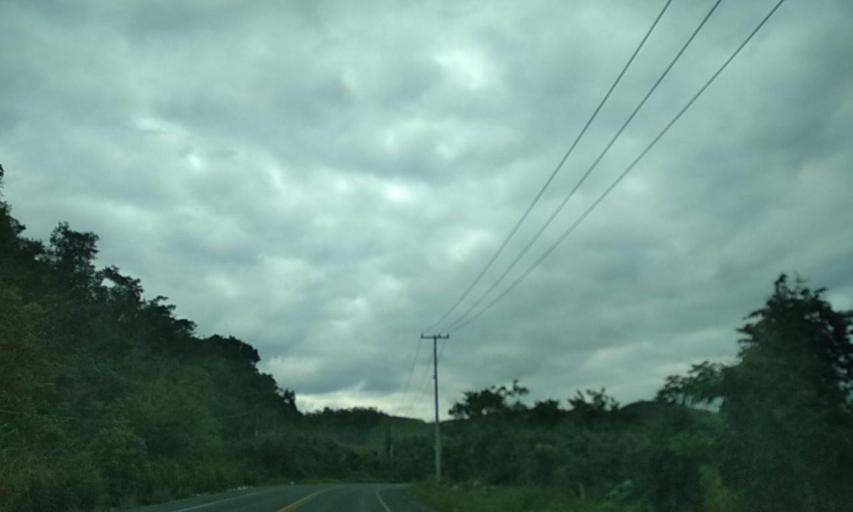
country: MX
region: Veracruz
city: Papantla de Olarte
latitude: 20.4687
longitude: -97.3197
